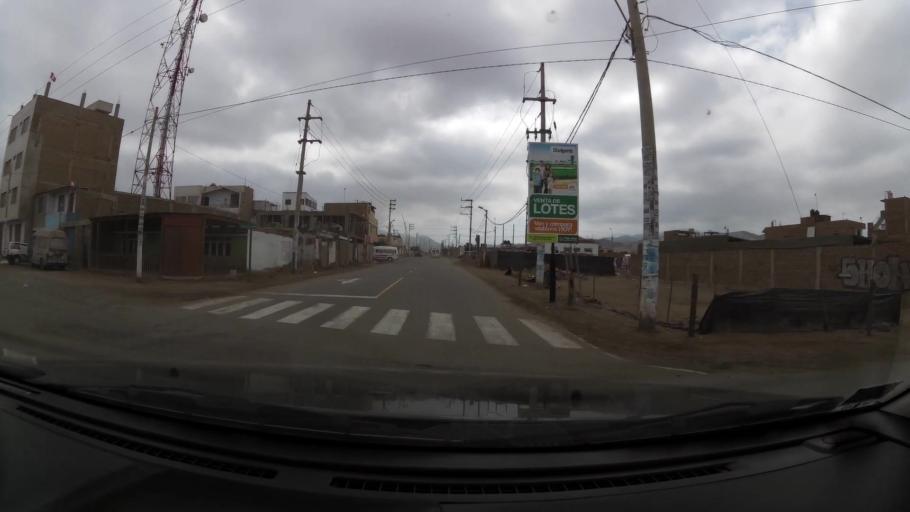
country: PE
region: Lima
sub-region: Provincia de Canete
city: Chilca
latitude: -12.5131
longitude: -76.7372
